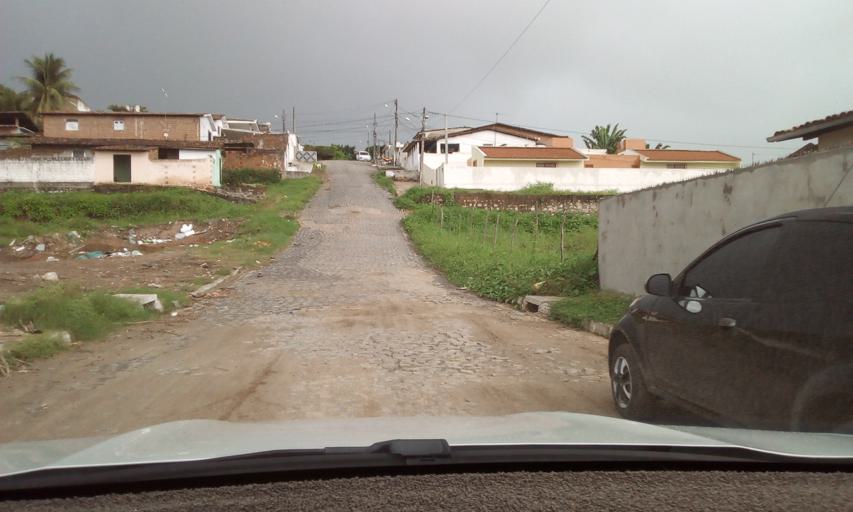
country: BR
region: Paraiba
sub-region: Bayeux
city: Bayeux
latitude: -7.1578
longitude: -34.9020
